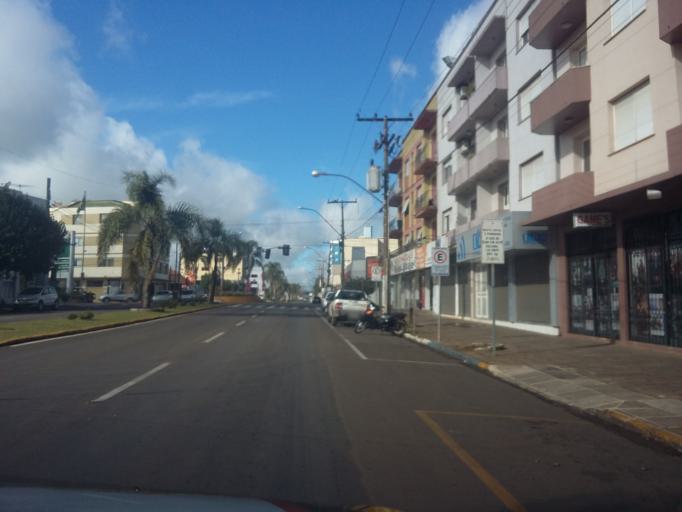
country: BR
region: Rio Grande do Sul
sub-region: Vacaria
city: Vacaria
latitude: -28.5096
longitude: -50.9360
